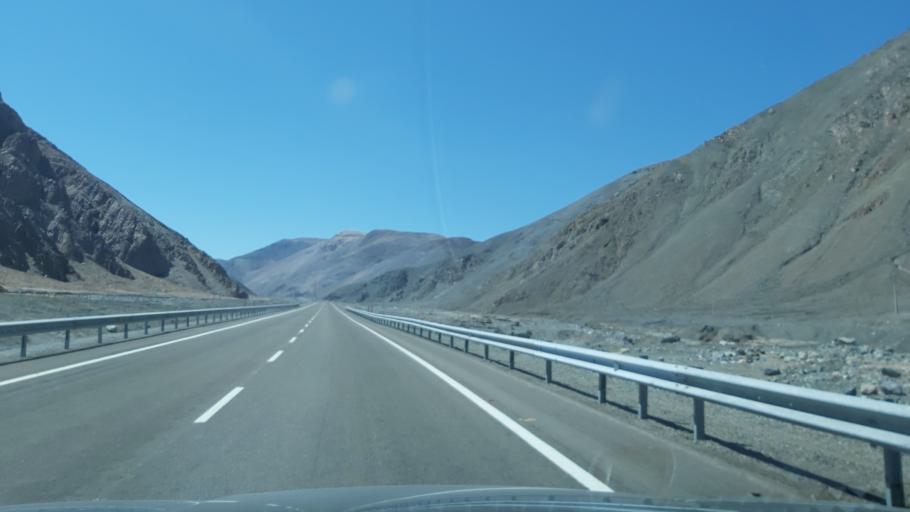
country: CL
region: Atacama
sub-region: Provincia de Chanaral
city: Diego de Almagro
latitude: -26.3498
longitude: -69.7394
